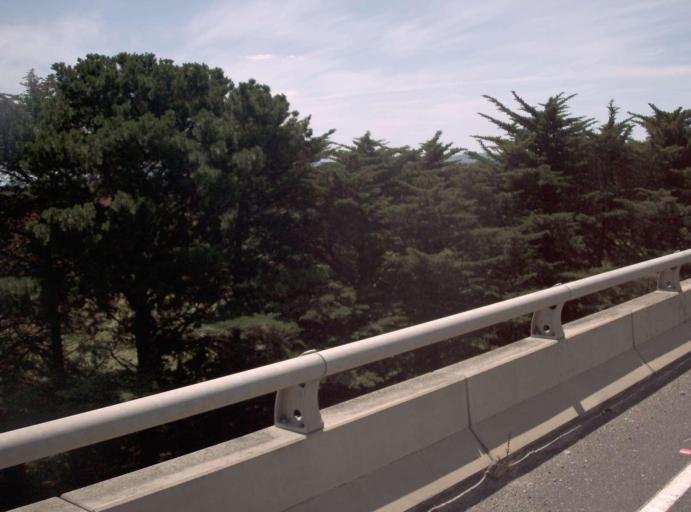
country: AU
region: Victoria
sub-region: Latrobe
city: Morwell
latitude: -38.2298
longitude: 146.4567
